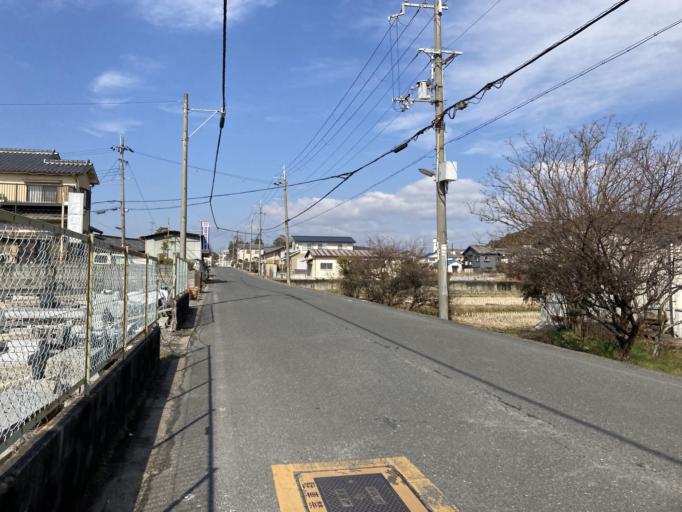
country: JP
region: Nara
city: Nara-shi
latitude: 34.6949
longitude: 135.8065
